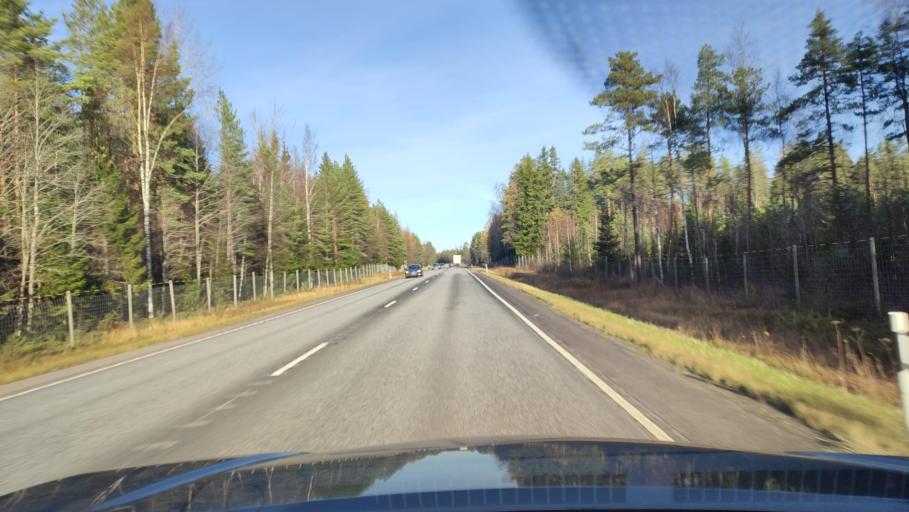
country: FI
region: Ostrobothnia
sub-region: Vaasa
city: Malax
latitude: 62.8323
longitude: 21.6938
